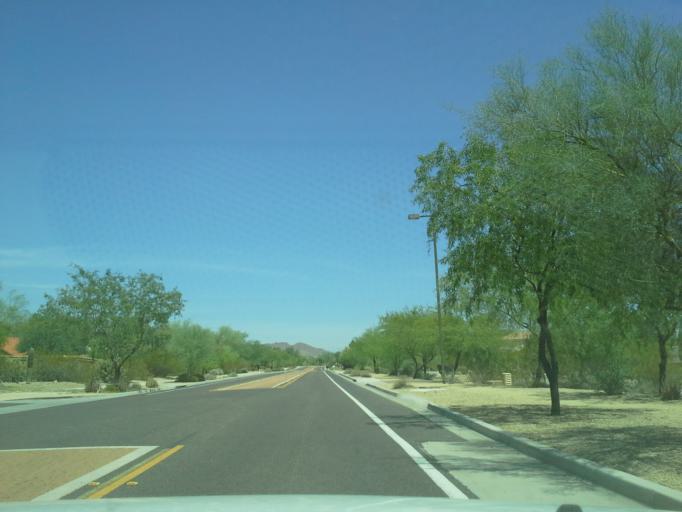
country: US
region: Arizona
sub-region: Maricopa County
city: Scottsdale
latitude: 33.5970
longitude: -111.8527
